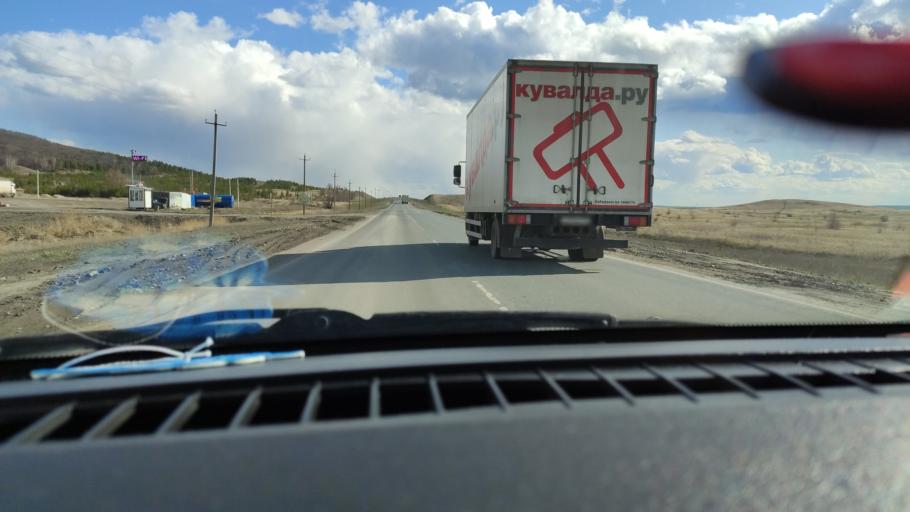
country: RU
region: Saratov
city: Alekseyevka
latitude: 52.3032
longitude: 47.9265
